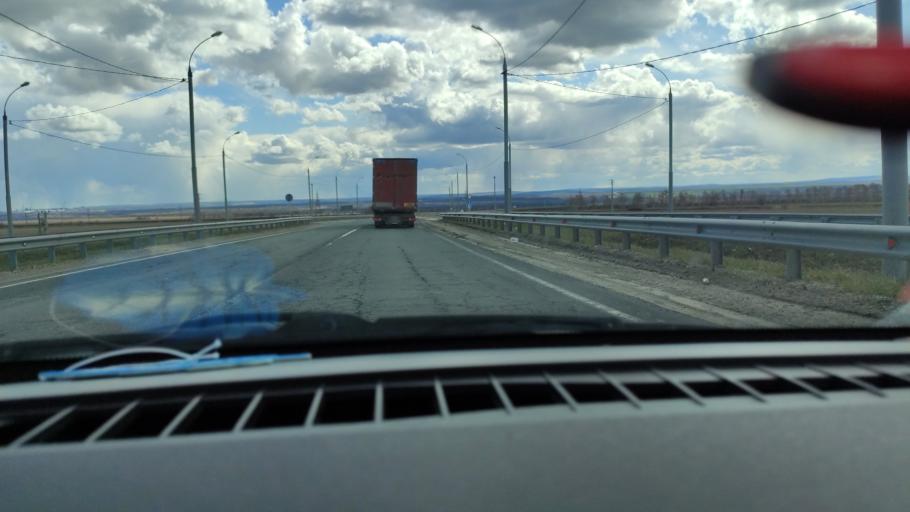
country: RU
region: Samara
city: Varlamovo
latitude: 53.1898
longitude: 48.2920
